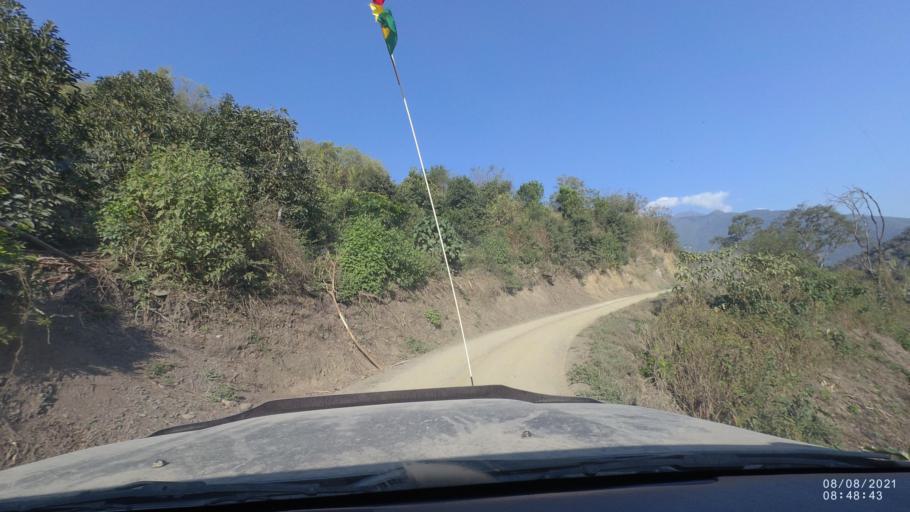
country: BO
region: La Paz
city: Quime
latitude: -16.5312
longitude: -66.7554
